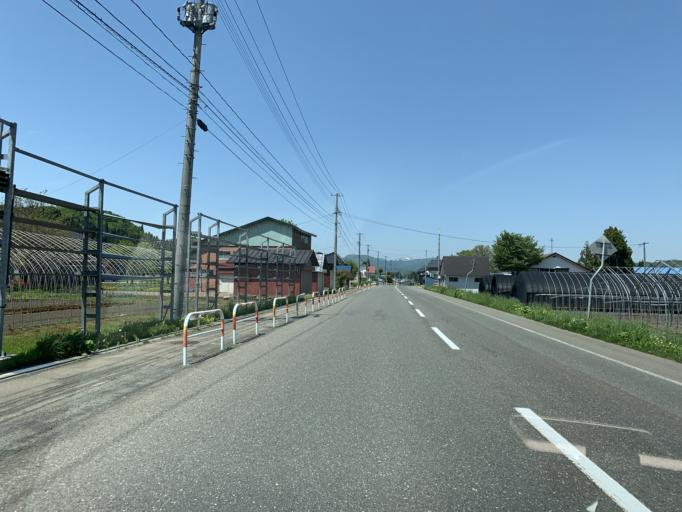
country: JP
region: Akita
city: Yokotemachi
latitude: 39.3835
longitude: 140.7584
